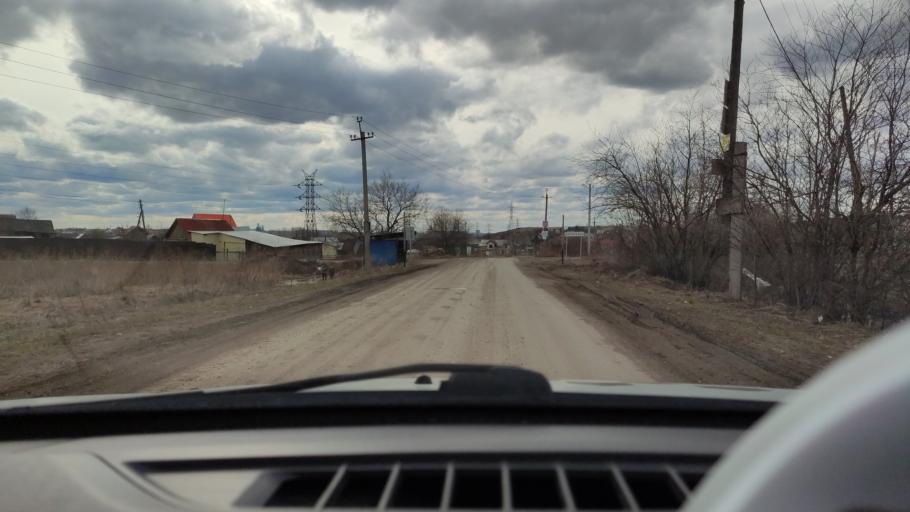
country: RU
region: Perm
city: Froly
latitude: 57.9300
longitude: 56.2418
